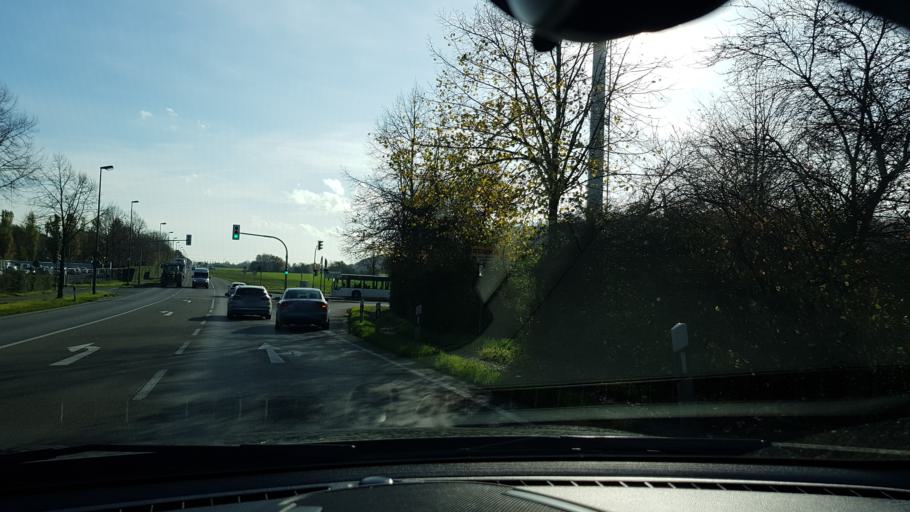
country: DE
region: North Rhine-Westphalia
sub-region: Regierungsbezirk Dusseldorf
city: Grevenbroich
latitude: 51.0818
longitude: 6.6119
